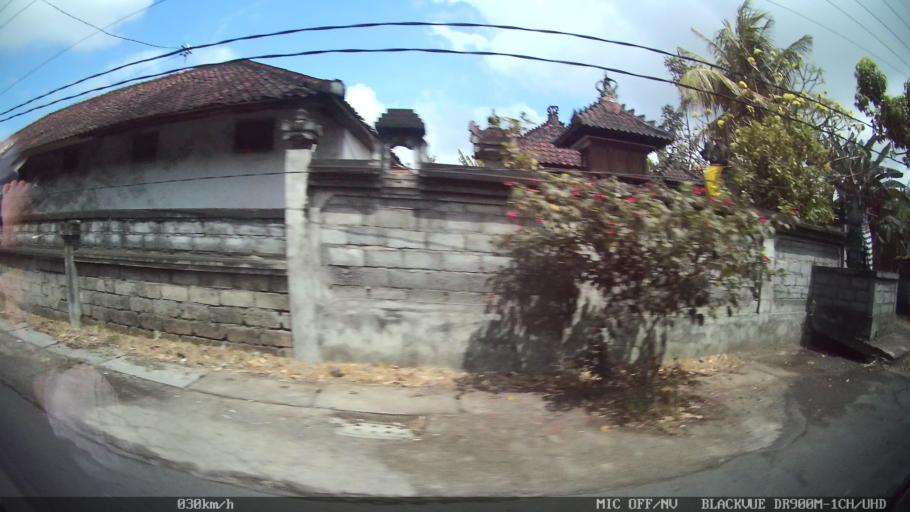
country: ID
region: Bali
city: Banjar Pasekan
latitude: -8.6001
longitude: 115.2914
